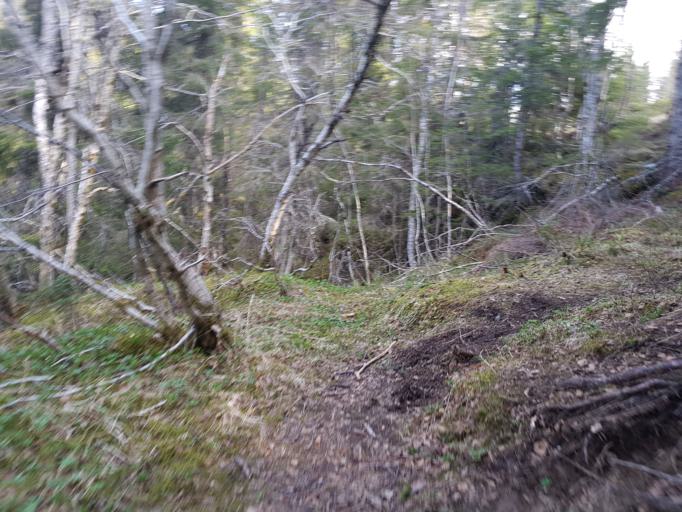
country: NO
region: Sor-Trondelag
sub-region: Trondheim
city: Trondheim
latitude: 63.4398
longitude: 10.2902
